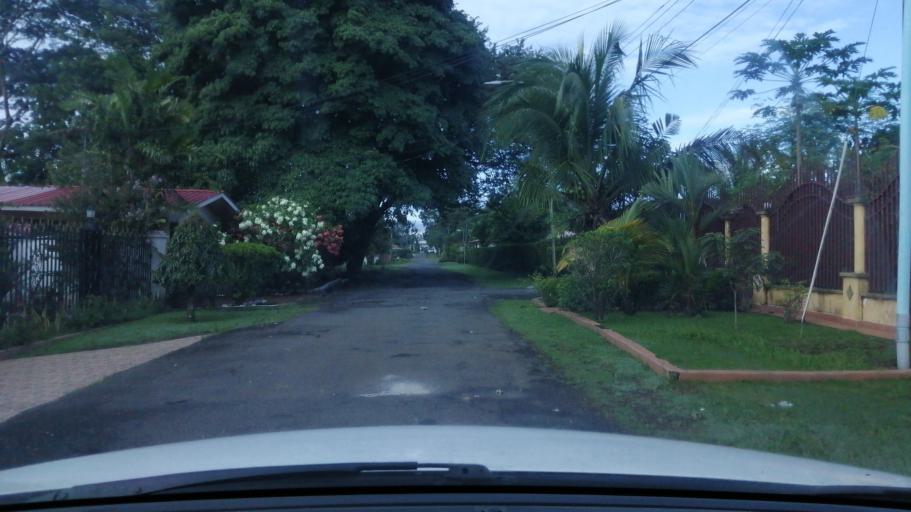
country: PA
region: Chiriqui
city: Mata del Nance
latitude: 8.4508
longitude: -82.4177
